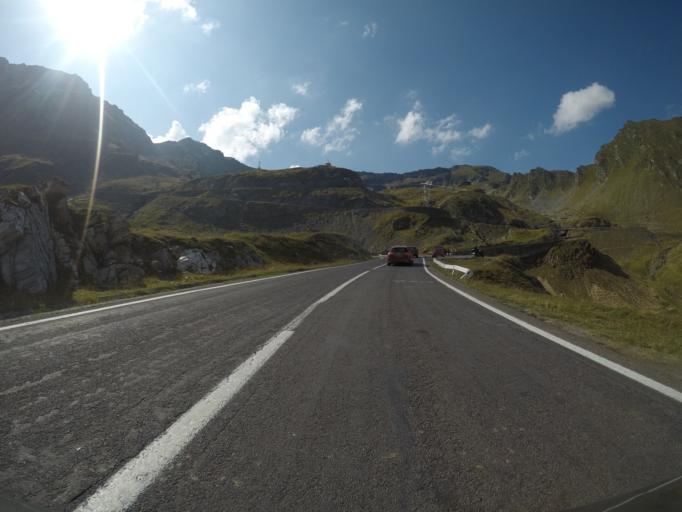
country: RO
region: Sibiu
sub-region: Comuna Cartisoara
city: Cartisoara
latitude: 45.6087
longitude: 24.6177
